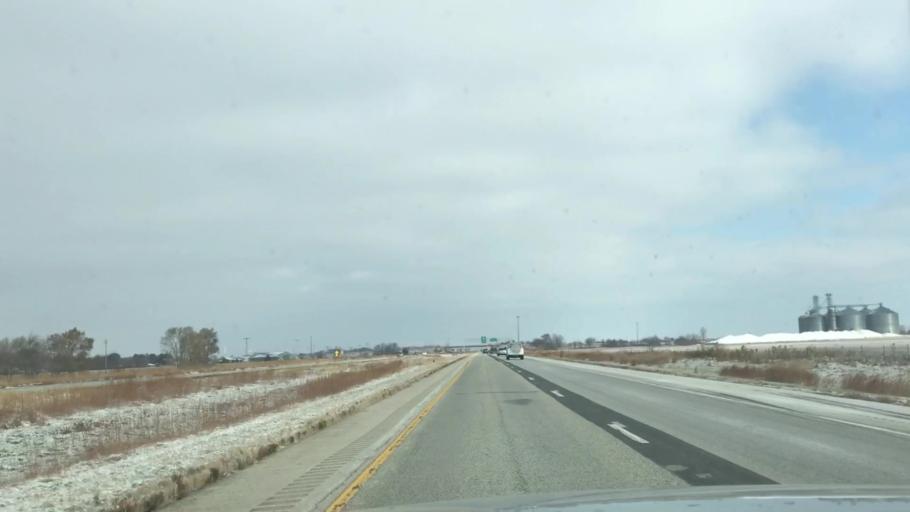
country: US
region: Illinois
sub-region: Sangamon County
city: Divernon
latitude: 39.5580
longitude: -89.6460
